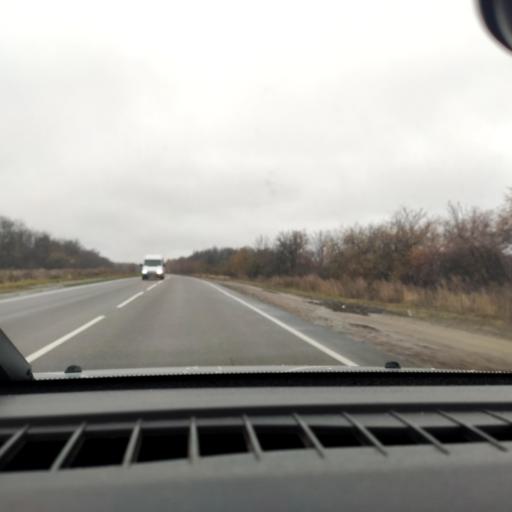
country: RU
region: Voronezj
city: Kolodeznyy
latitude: 51.3715
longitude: 39.0228
